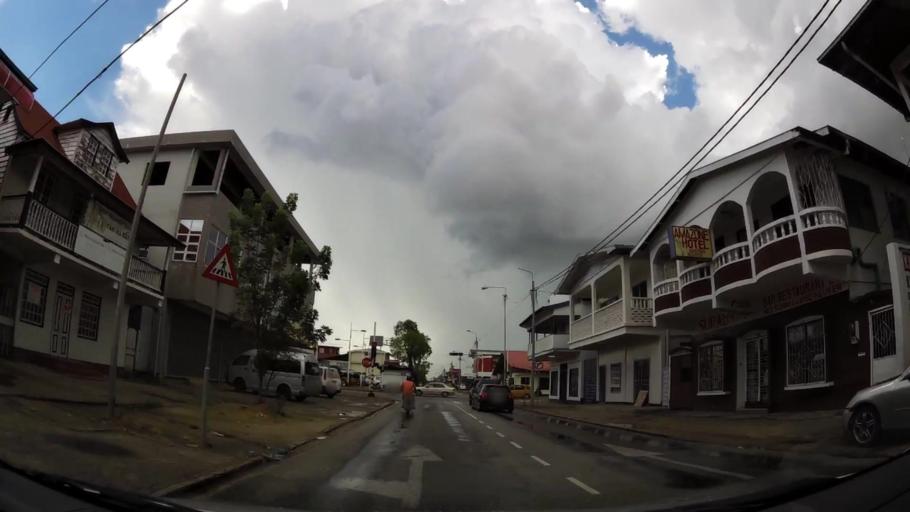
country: SR
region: Paramaribo
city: Paramaribo
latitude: 5.8306
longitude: -55.1639
